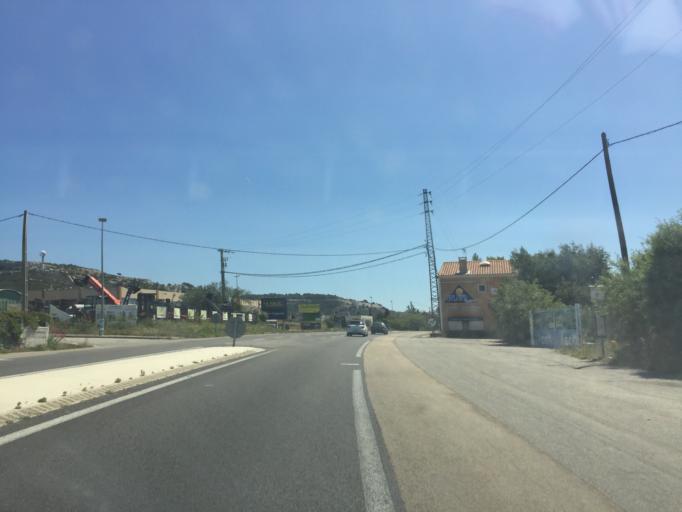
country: FR
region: Provence-Alpes-Cote d'Azur
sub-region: Departement des Bouches-du-Rhone
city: Rognac
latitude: 43.4792
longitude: 5.2271
